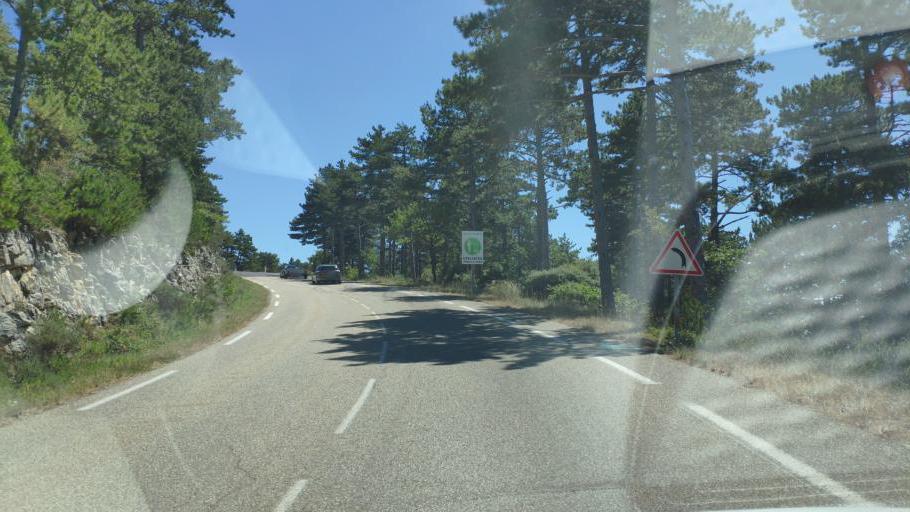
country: FR
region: Provence-Alpes-Cote d'Azur
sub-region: Departement du Vaucluse
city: Malaucene
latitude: 44.1572
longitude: 5.1471
